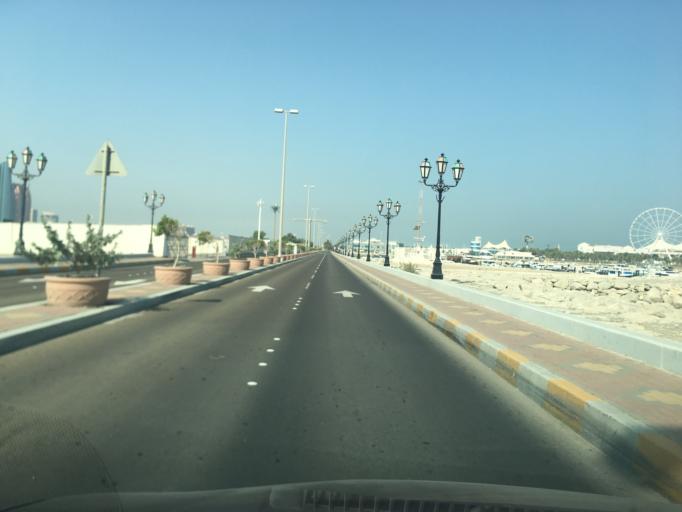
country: AE
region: Abu Dhabi
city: Abu Dhabi
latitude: 24.4764
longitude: 54.3297
